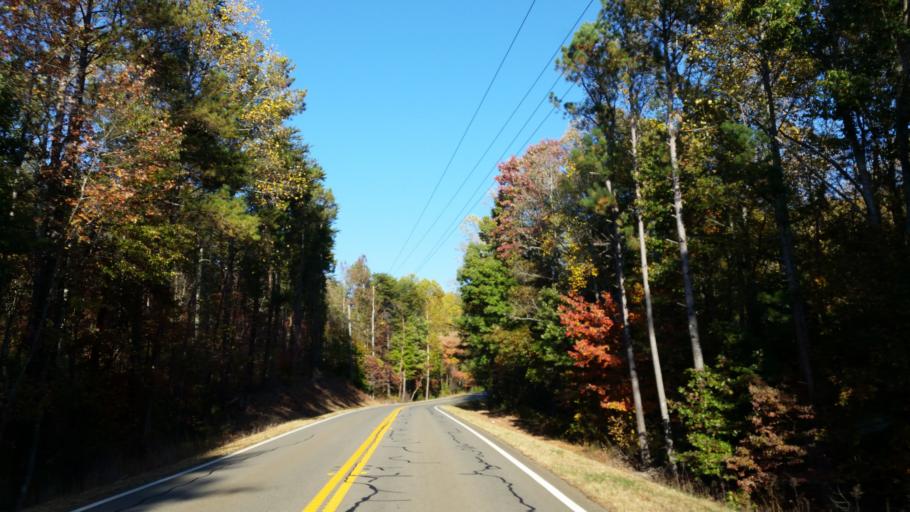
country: US
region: Georgia
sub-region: Pickens County
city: Jasper
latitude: 34.5223
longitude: -84.4848
